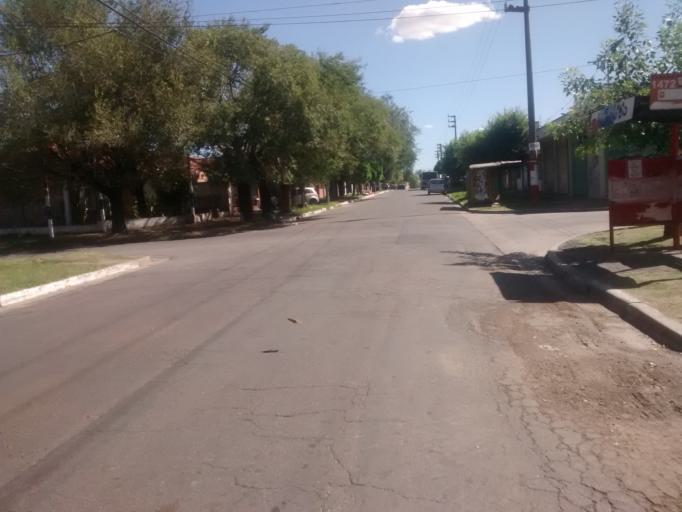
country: AR
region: Buenos Aires
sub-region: Partido de La Plata
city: La Plata
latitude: -34.9319
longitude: -57.9045
